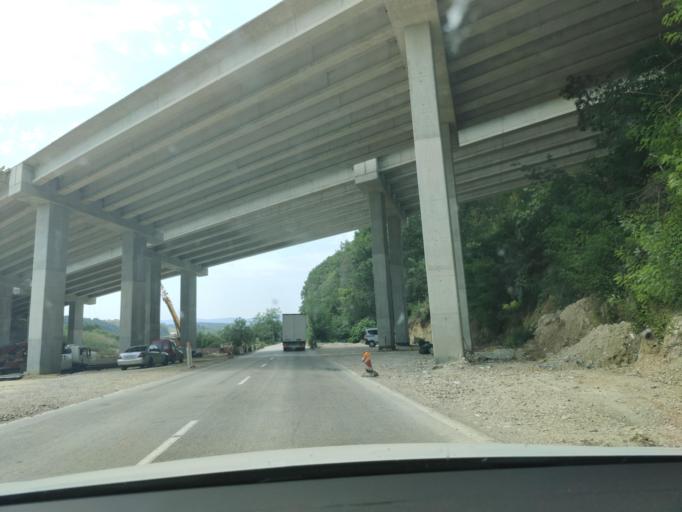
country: BG
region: Vidin
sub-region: Obshtina Dimovo
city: Dimovo
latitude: 43.7581
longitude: 22.7443
